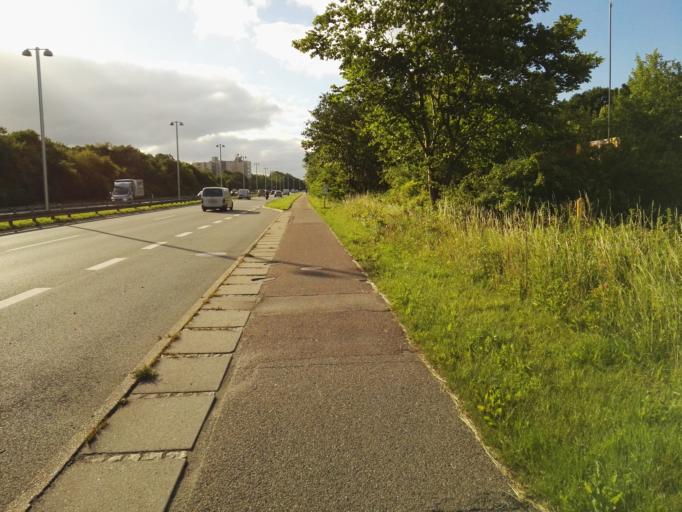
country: DK
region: Capital Region
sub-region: Egedal Kommune
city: Smorumnedre
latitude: 55.7508
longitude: 12.3088
